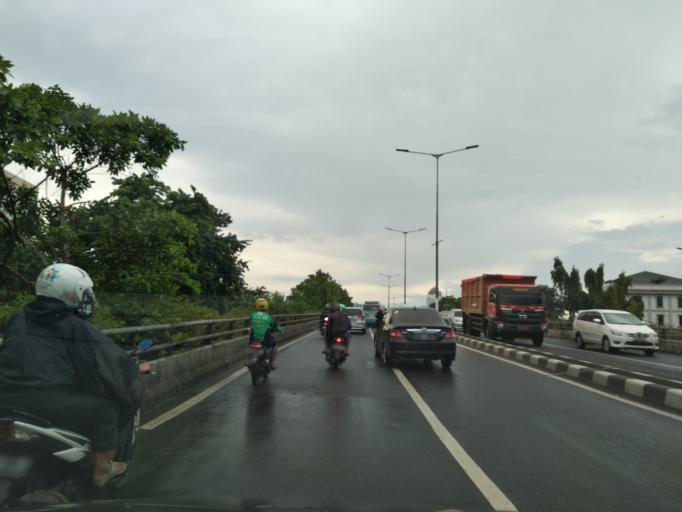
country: ID
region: Jakarta Raya
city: Jakarta
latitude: -6.2254
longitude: 106.8601
